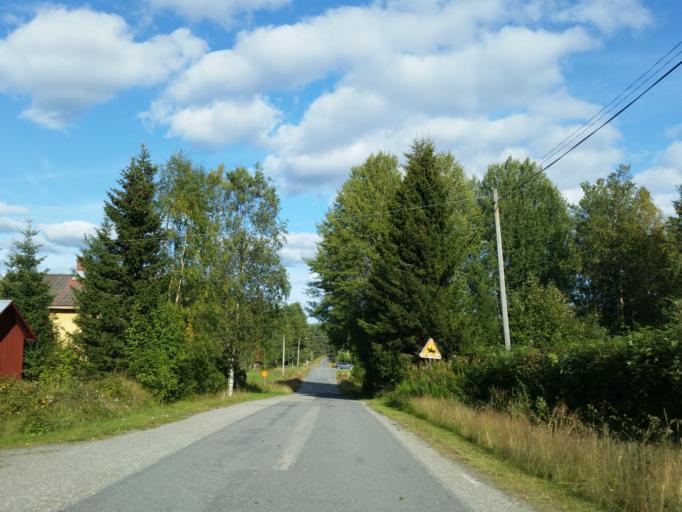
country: SE
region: Vaesterbotten
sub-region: Robertsfors Kommun
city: Robertsfors
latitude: 64.1710
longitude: 20.9412
